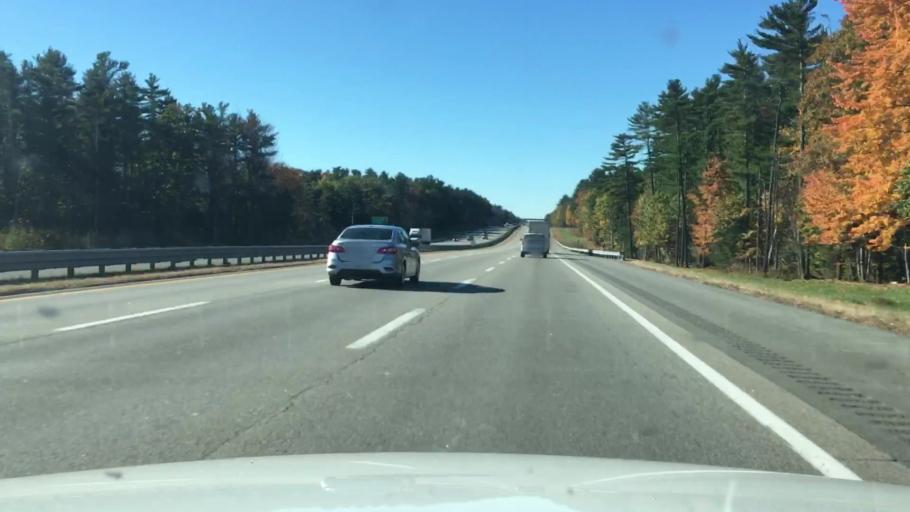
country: US
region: Maine
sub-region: Cumberland County
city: West Scarborough
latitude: 43.5656
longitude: -70.4128
